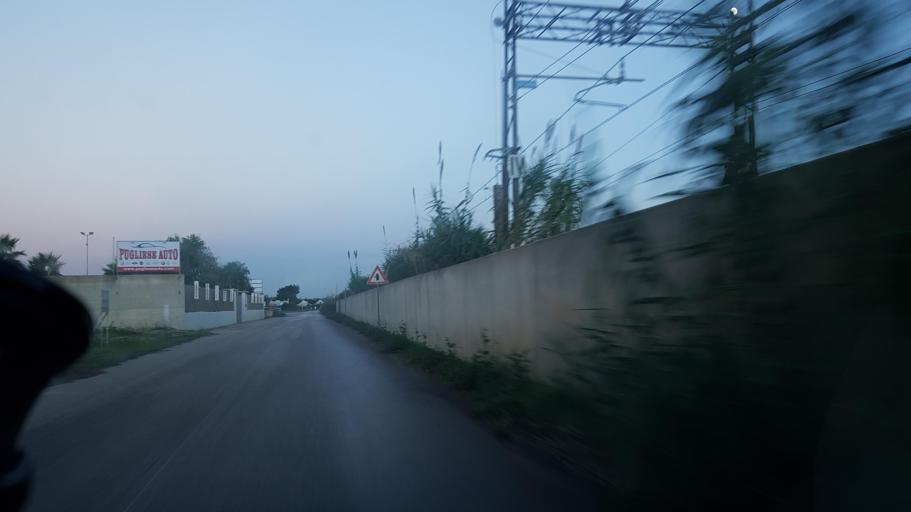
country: IT
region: Apulia
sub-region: Provincia di Brindisi
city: Latiano
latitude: 40.5590
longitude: 17.7256
